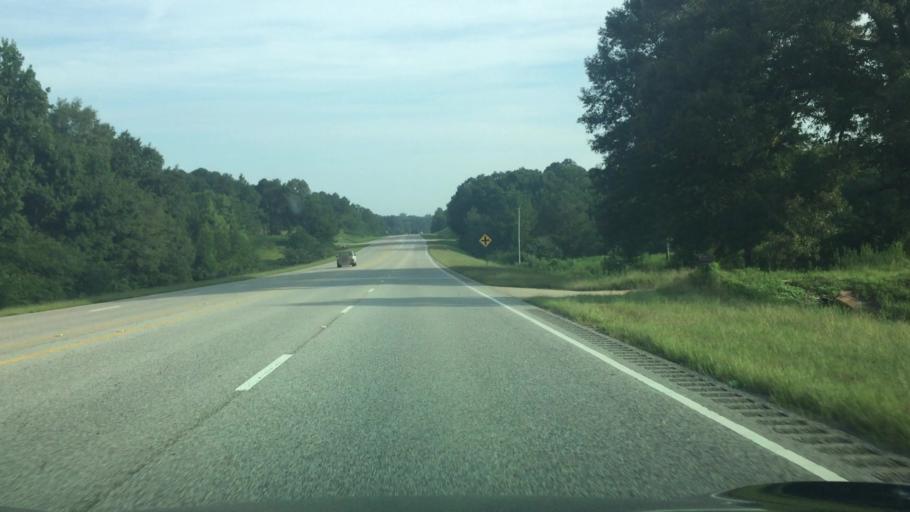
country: US
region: Alabama
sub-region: Covington County
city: Andalusia
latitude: 31.4127
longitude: -86.6065
